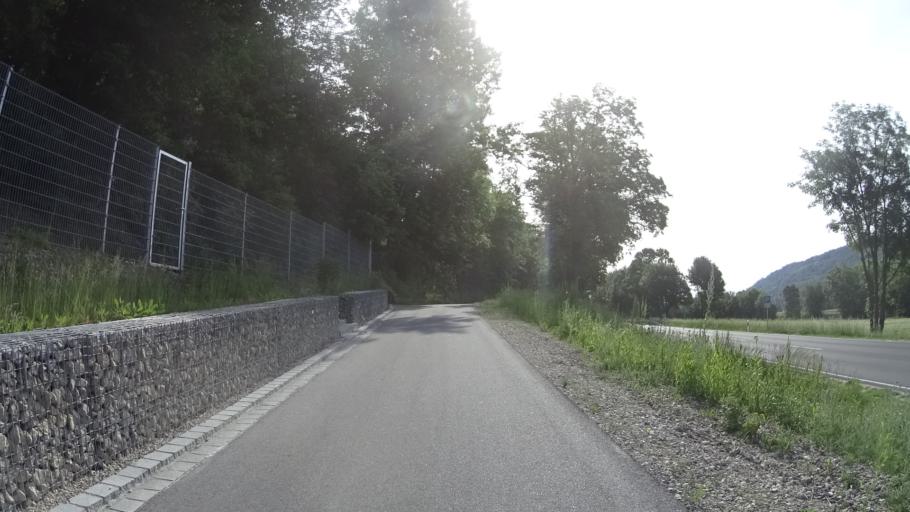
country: DE
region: Bavaria
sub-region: Lower Bavaria
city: Ihrlerstein
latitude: 48.9260
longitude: 11.8363
